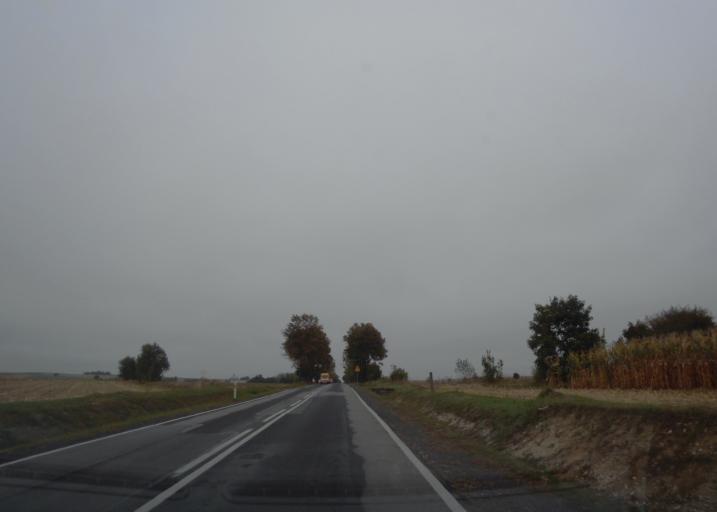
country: PL
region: Lublin Voivodeship
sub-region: Powiat chelmski
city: Rejowiec
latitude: 51.0367
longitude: 23.2459
